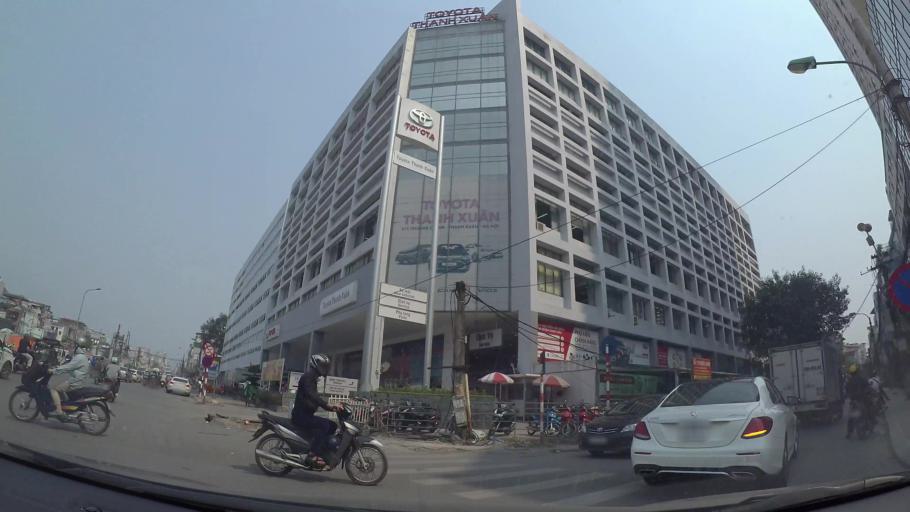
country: VN
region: Ha Noi
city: Dong Da
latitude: 21.0023
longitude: 105.8227
